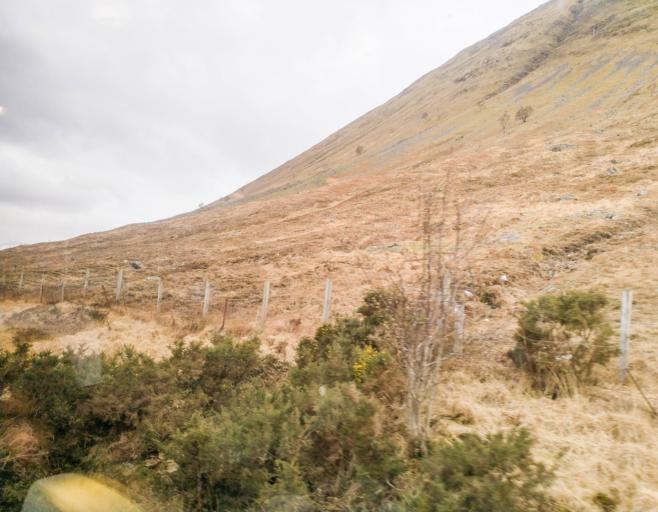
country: GB
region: Scotland
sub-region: Argyll and Bute
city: Garelochhead
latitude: 56.4883
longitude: -4.7244
